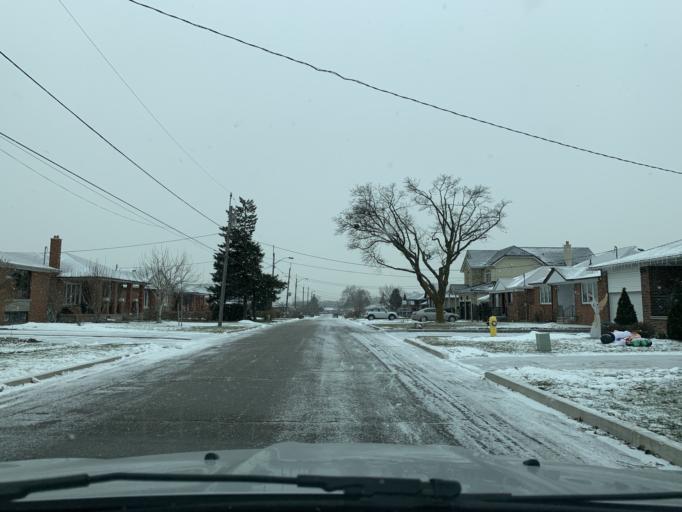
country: CA
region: Ontario
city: Concord
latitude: 43.7339
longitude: -79.4900
